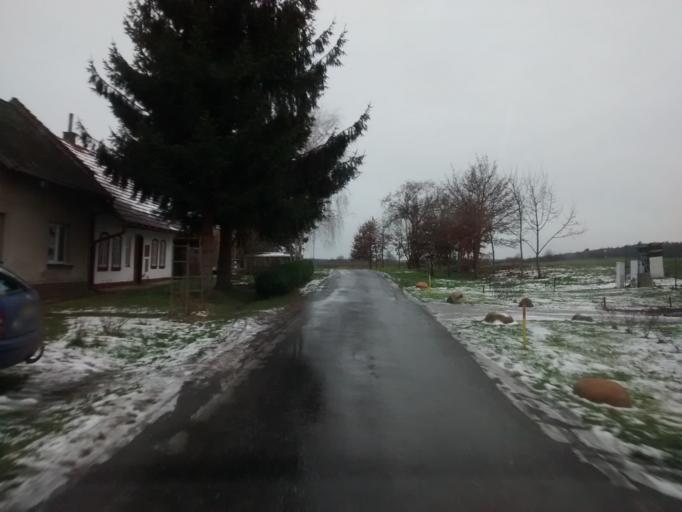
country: CZ
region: Central Bohemia
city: Rozd'alovice
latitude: 50.3091
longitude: 15.1701
